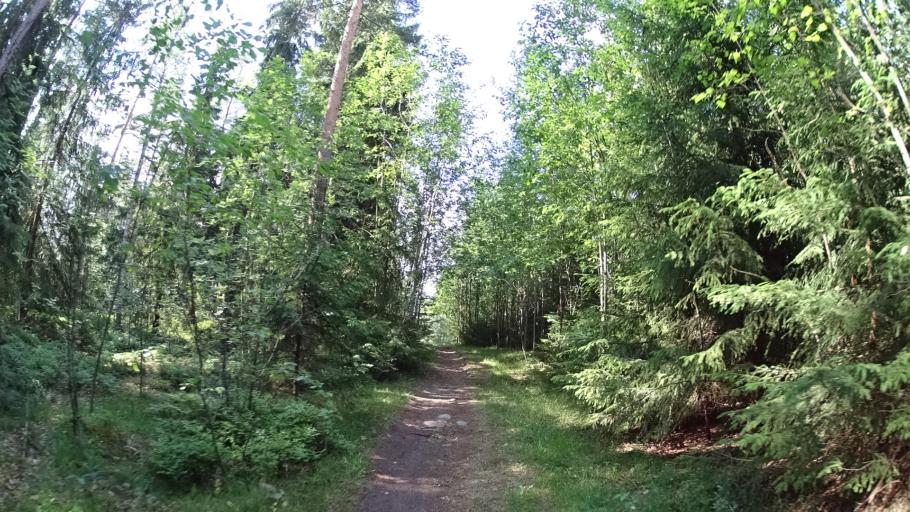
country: FI
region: Uusimaa
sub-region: Helsinki
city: Teekkarikylae
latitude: 60.2884
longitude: 24.9002
